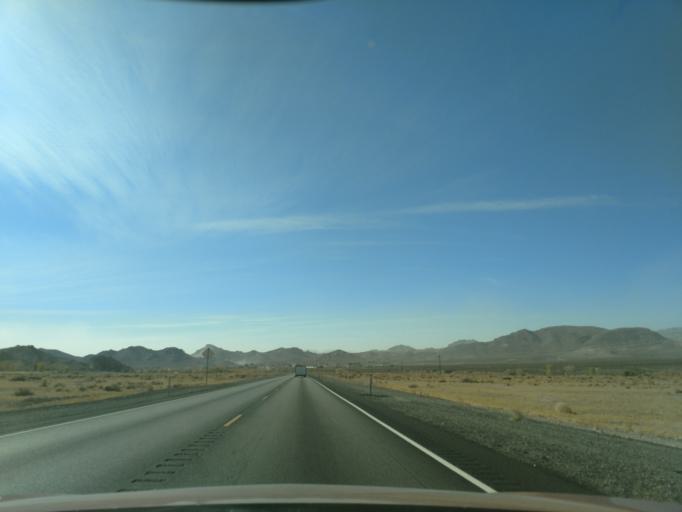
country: US
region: Nevada
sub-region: Nye County
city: Beatty
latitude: 36.9232
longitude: -116.7419
